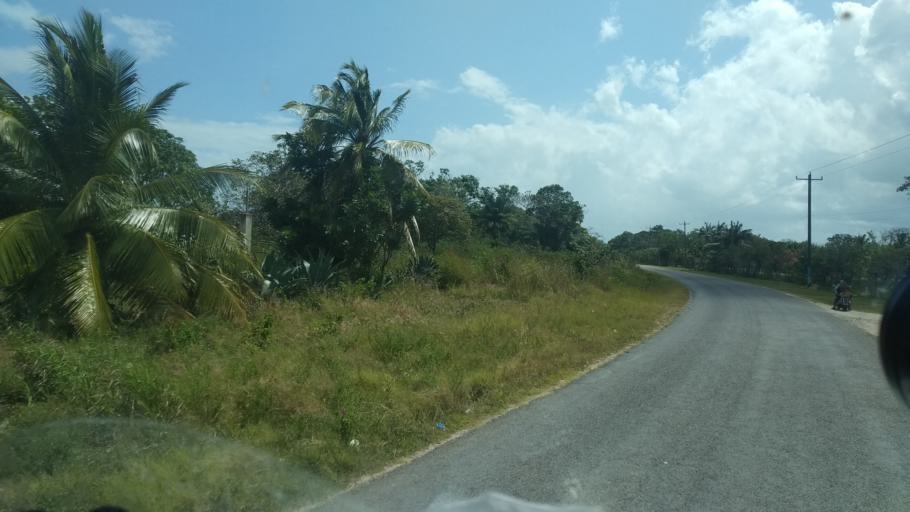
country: BZ
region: Corozal
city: Corozal
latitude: 18.3903
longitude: -88.4204
